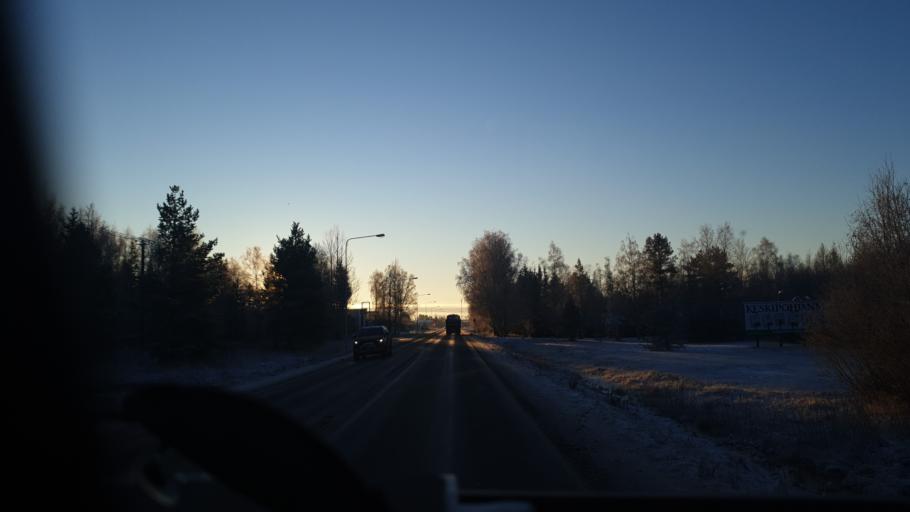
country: FI
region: Northern Ostrobothnia
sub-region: Ylivieska
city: Kalajoki
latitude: 64.2700
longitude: 23.9491
